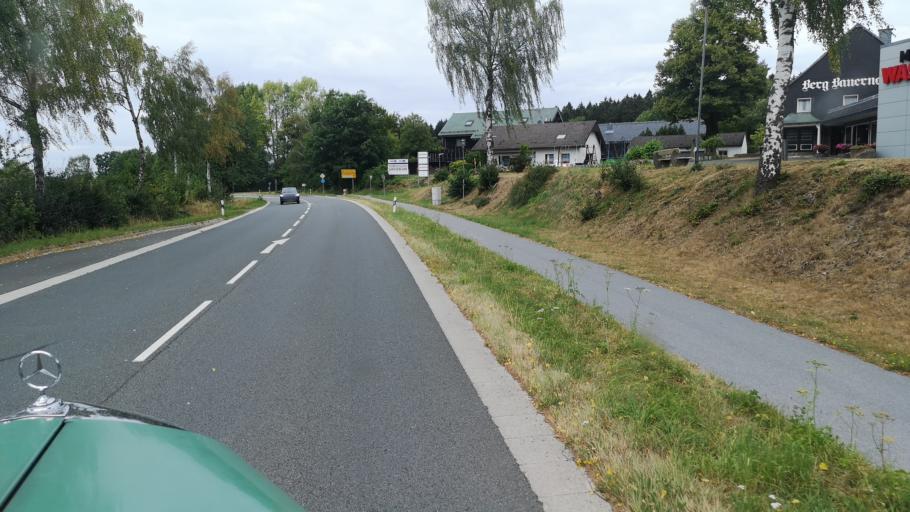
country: DE
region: North Rhine-Westphalia
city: Wipperfurth
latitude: 51.1053
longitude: 7.3678
